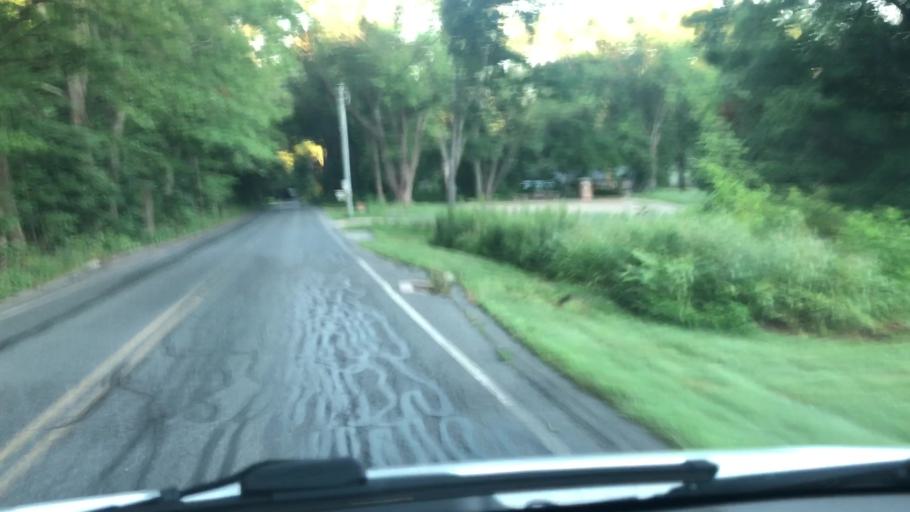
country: US
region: Massachusetts
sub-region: Hampshire County
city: Southampton
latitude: 42.2406
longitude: -72.7011
